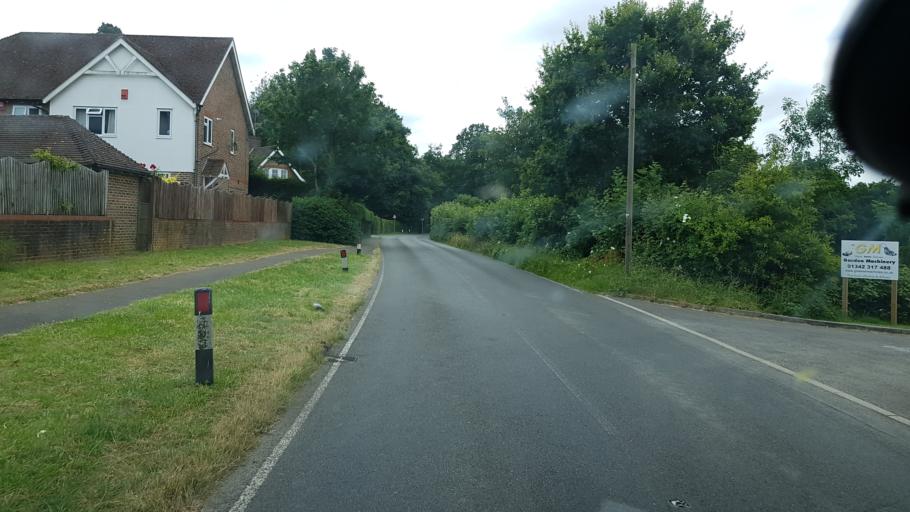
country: GB
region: England
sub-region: Surrey
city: Felbridge
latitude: 51.1274
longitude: -0.0339
